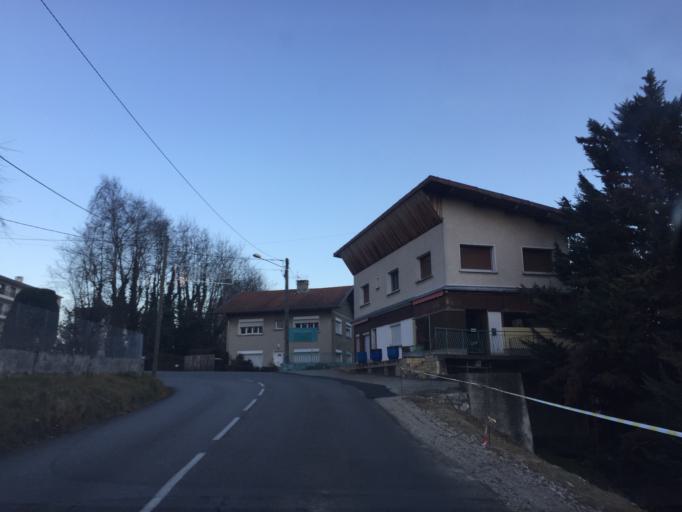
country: FR
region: Rhone-Alpes
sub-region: Departement de la Savoie
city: Tresserve
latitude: 45.6790
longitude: 5.9024
